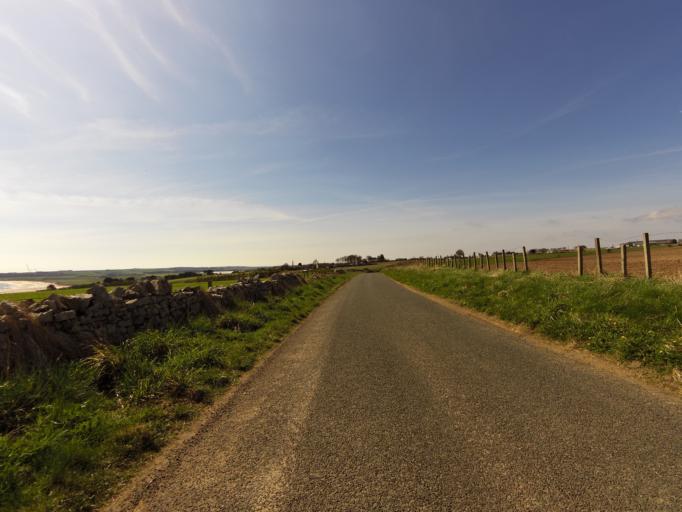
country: GB
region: Scotland
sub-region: Angus
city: Montrose
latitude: 56.6681
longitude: -2.5027
